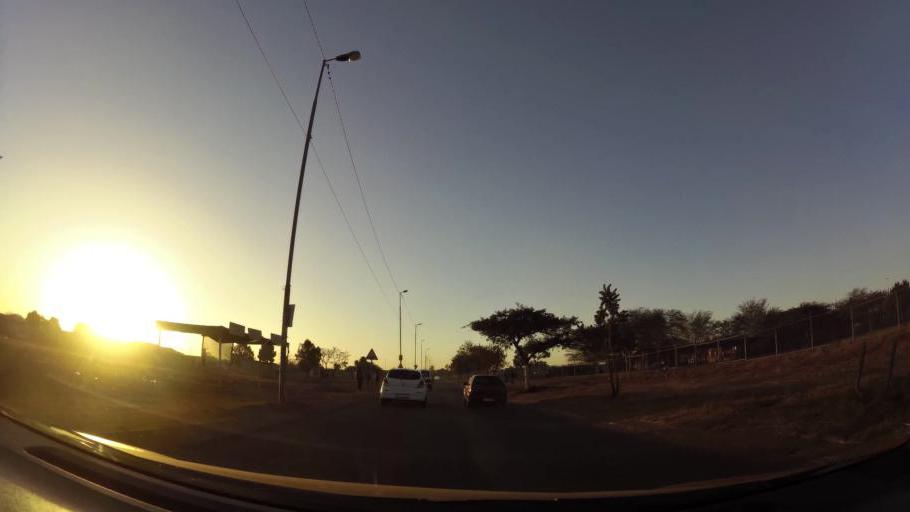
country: ZA
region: Gauteng
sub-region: City of Tshwane Metropolitan Municipality
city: Mabopane
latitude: -25.5832
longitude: 28.0884
